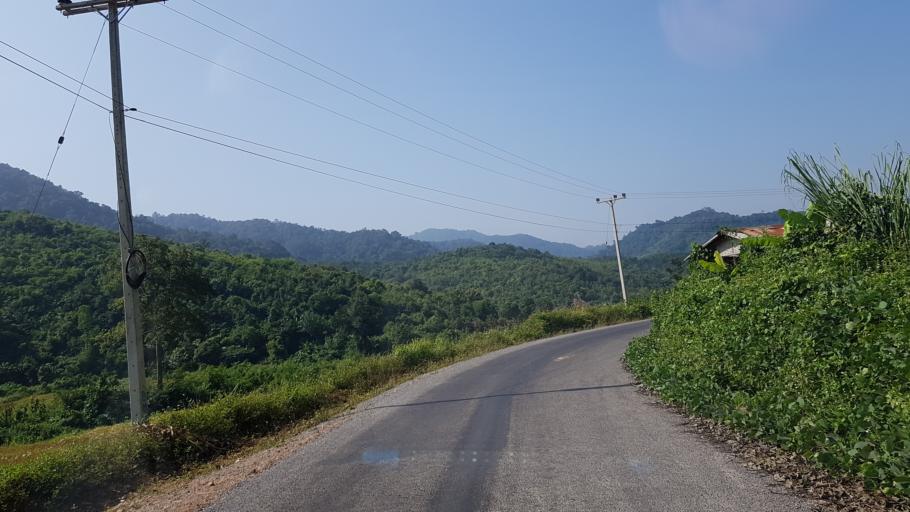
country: LA
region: Oudomxai
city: Muang Xay
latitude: 20.7124
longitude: 102.0635
